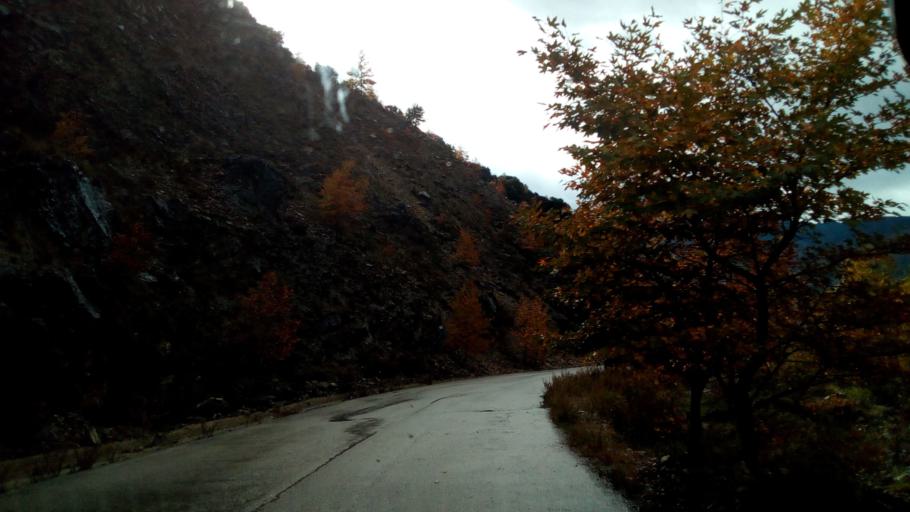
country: GR
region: West Greece
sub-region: Nomos Aitolias kai Akarnanias
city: Thermo
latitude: 38.6842
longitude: 21.8486
